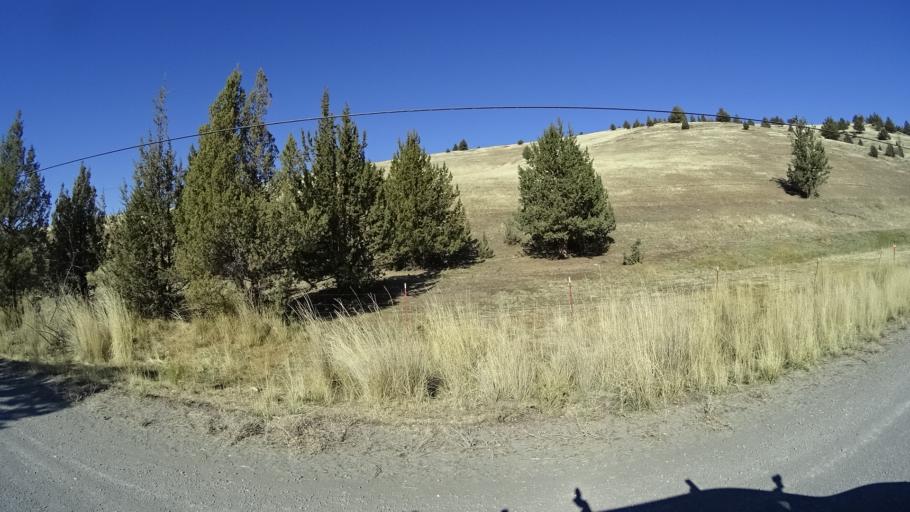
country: US
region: California
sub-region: Siskiyou County
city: Montague
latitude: 41.7305
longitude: -122.3574
